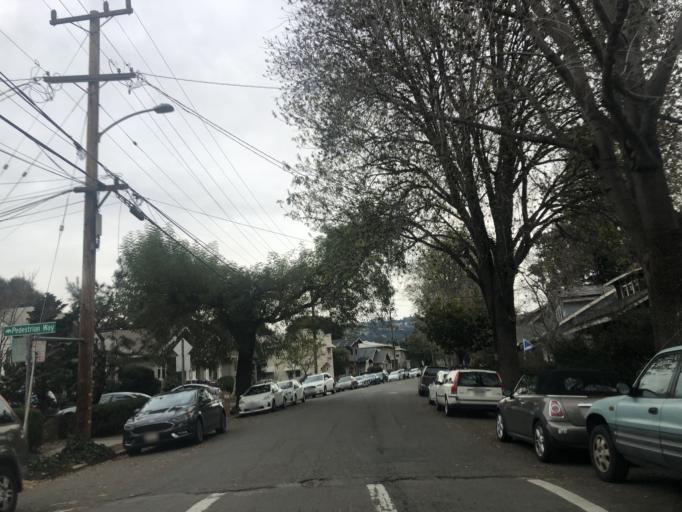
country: US
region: California
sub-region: Alameda County
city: Piedmont
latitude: 37.8451
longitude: -122.2543
